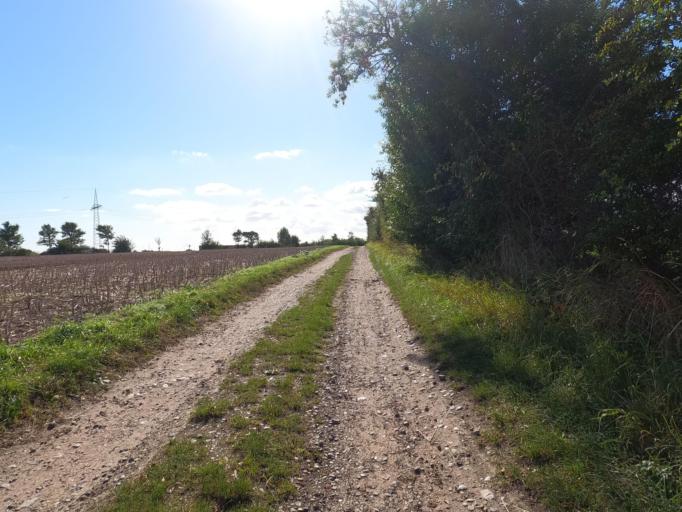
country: DE
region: Schleswig-Holstein
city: Grossenbrode
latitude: 54.3862
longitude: 11.1048
